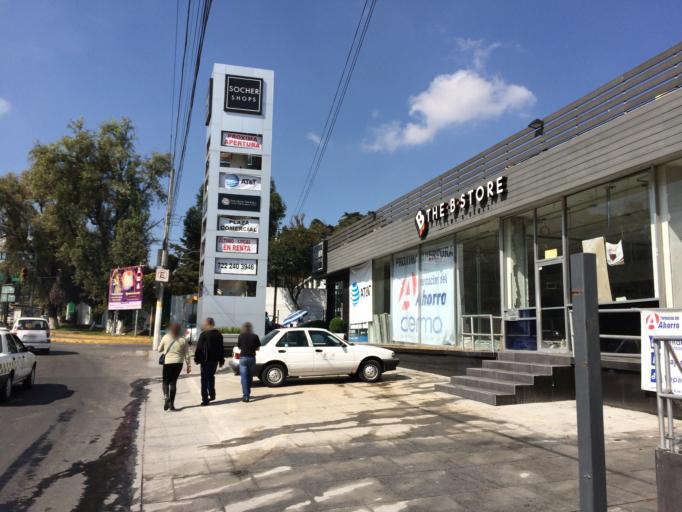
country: MX
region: Mexico
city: San Buenaventura
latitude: 19.2888
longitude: -99.6767
